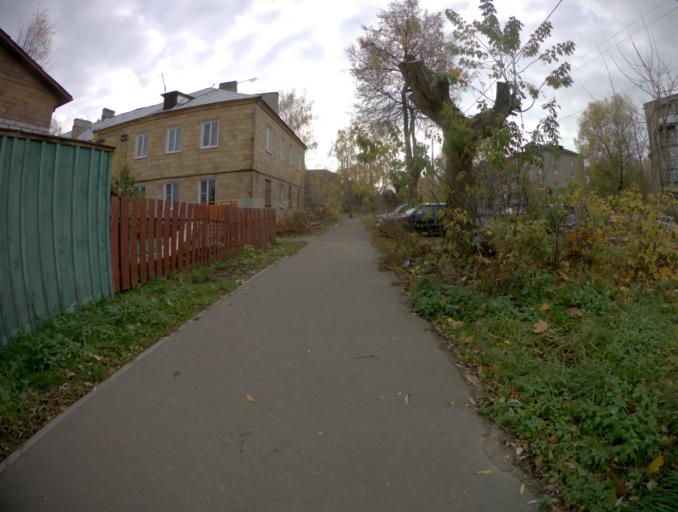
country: RU
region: Moskovskaya
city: Orekhovo-Zuyevo
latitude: 55.7981
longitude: 38.9537
